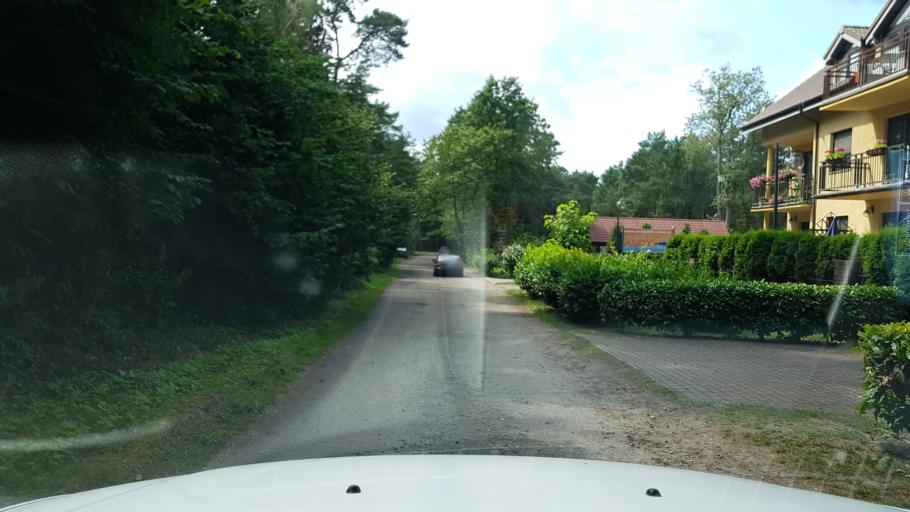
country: PL
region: West Pomeranian Voivodeship
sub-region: Powiat gryficki
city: Pobierowo
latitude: 54.0630
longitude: 14.9471
